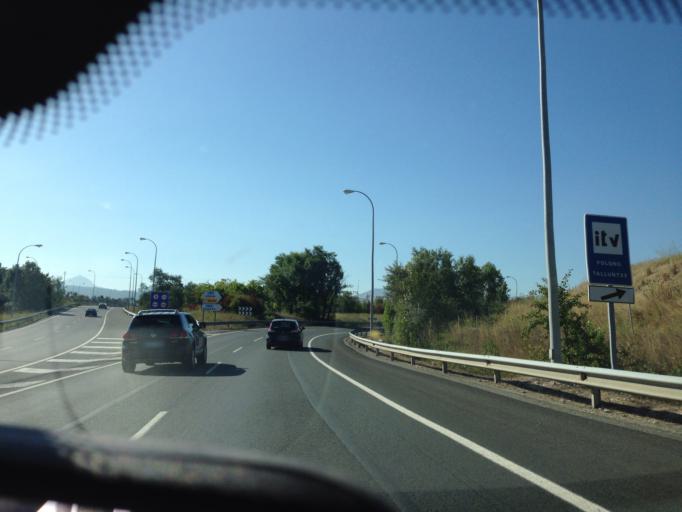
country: ES
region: Navarre
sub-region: Provincia de Navarra
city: Segundo Ensanche
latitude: 42.7800
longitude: -1.6350
